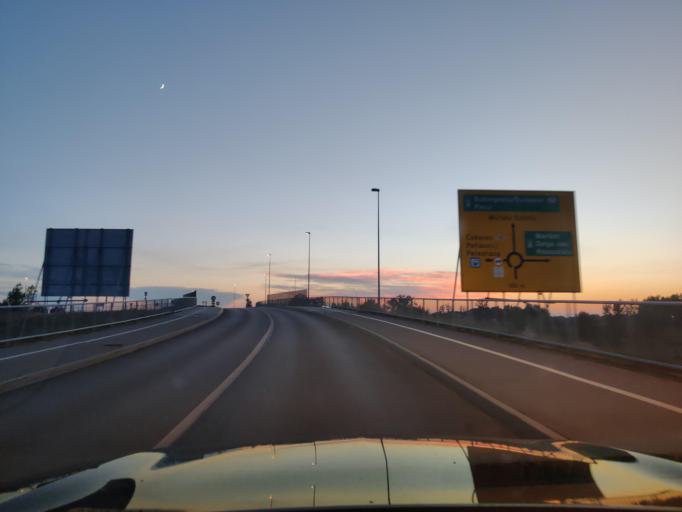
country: SI
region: Lendava-Lendva
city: Lendava
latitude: 46.5543
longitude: 16.4467
